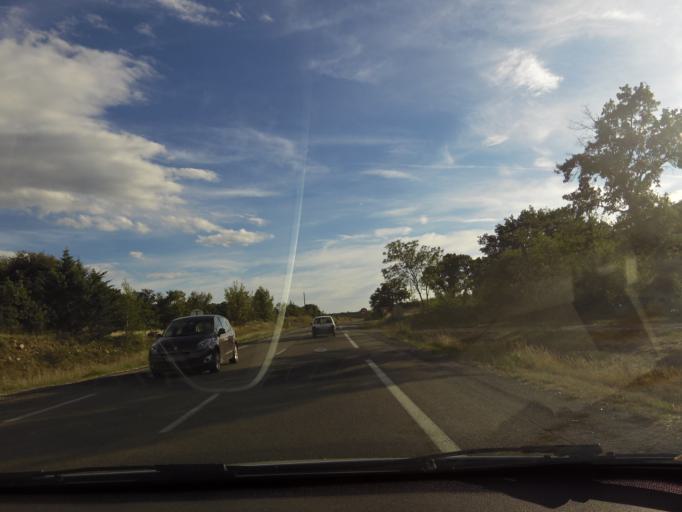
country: FR
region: Languedoc-Roussillon
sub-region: Departement du Gard
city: Quissac
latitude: 43.8893
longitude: 3.9781
